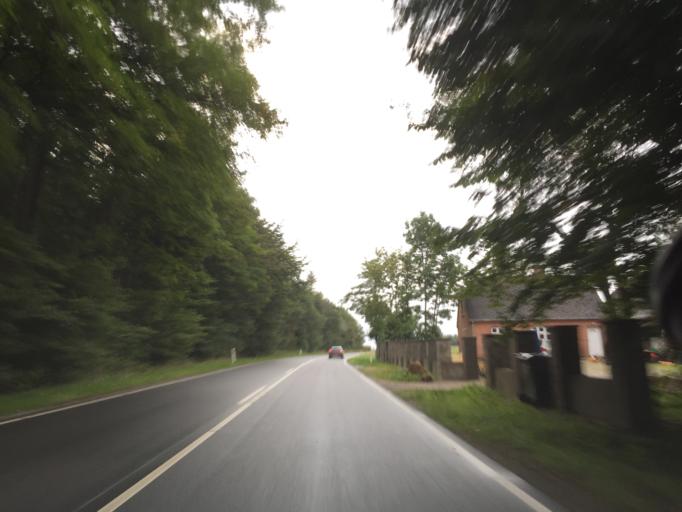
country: DK
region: Central Jutland
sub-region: Skanderborg Kommune
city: Skanderborg
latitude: 56.0805
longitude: 9.8989
